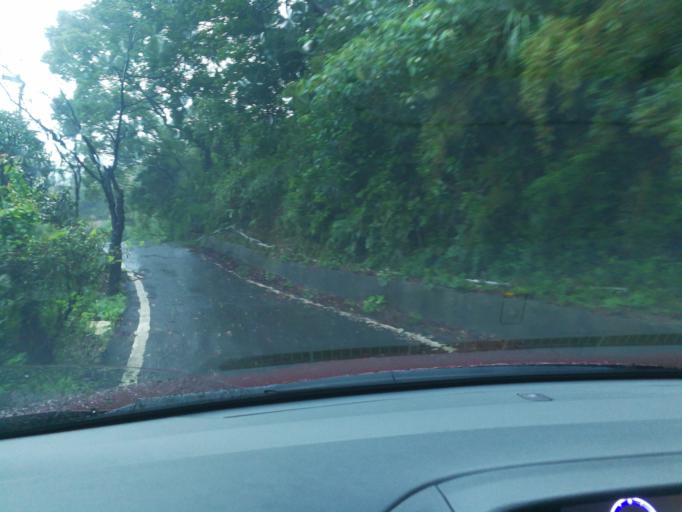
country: TW
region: Taipei
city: Taipei
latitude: 25.1118
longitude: 121.6247
